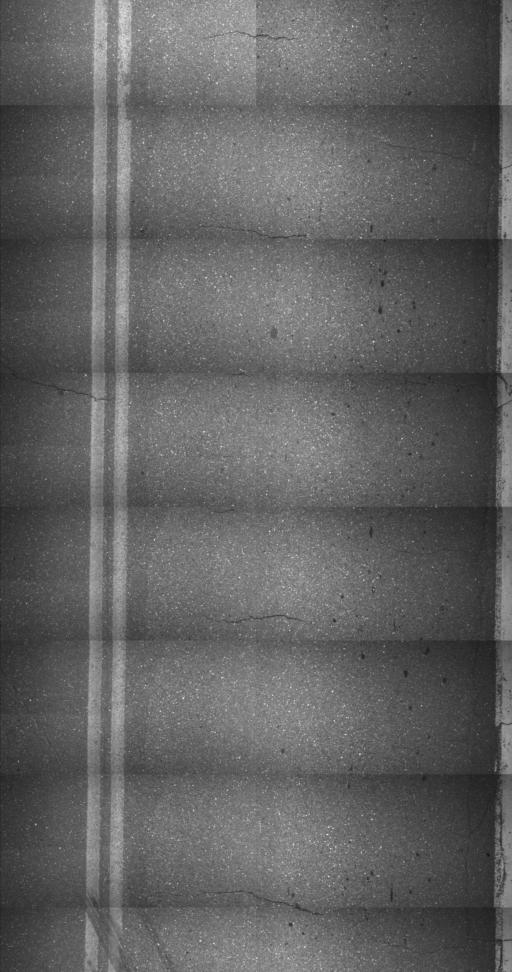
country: US
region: Vermont
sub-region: Orleans County
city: Newport
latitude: 44.8226
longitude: -72.2953
